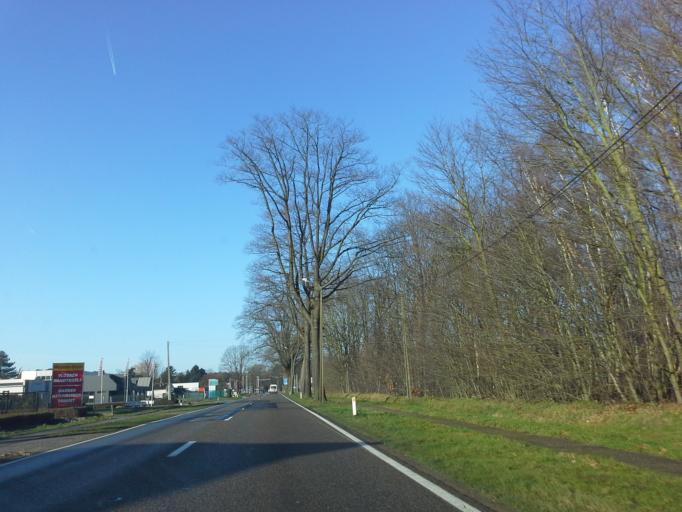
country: BE
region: Flanders
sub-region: Provincie Antwerpen
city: Olen
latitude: 51.1519
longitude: 4.9129
